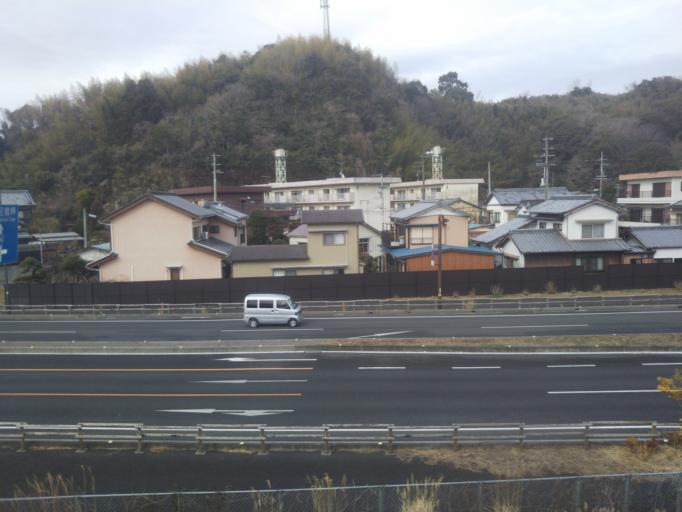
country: JP
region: Kochi
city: Nakamura
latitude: 32.9870
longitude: 132.9625
